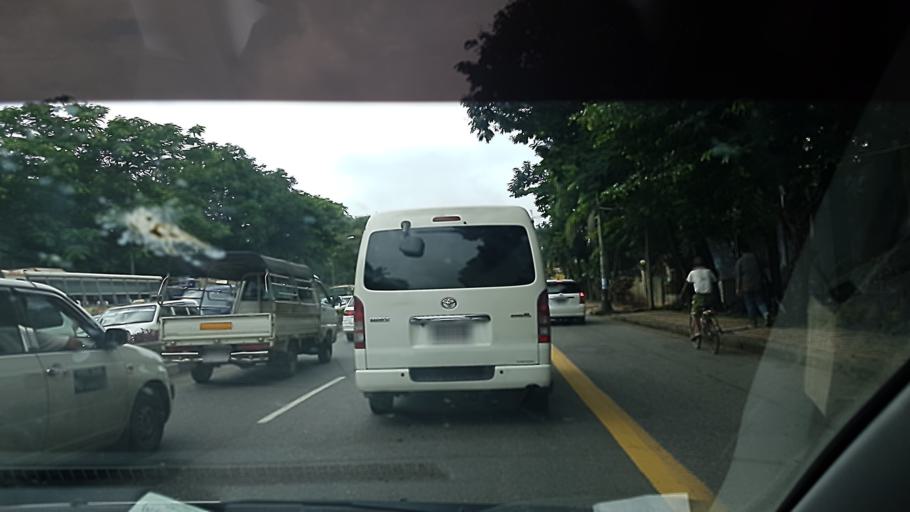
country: MM
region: Yangon
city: Yangon
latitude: 16.8107
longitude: 96.1353
